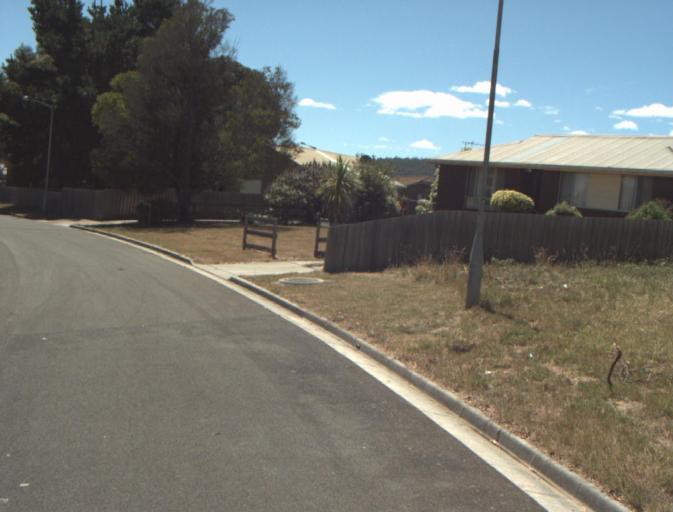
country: AU
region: Tasmania
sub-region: Launceston
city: Mayfield
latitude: -41.3770
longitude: 147.1392
